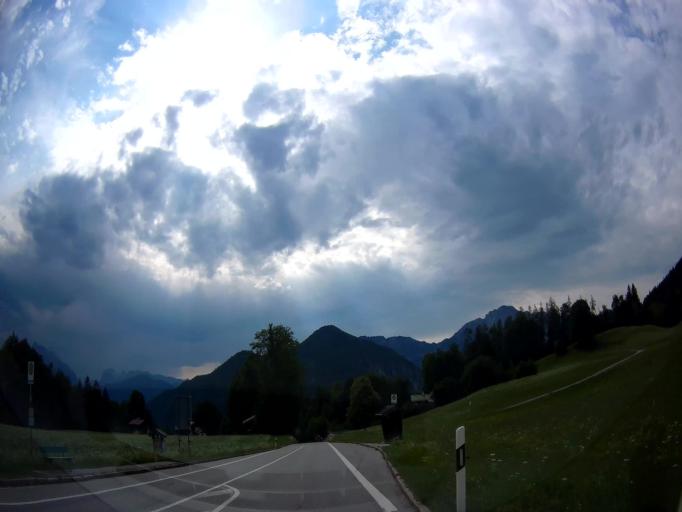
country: DE
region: Bavaria
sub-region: Upper Bavaria
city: Marktschellenberg
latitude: 47.6514
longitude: 13.0585
